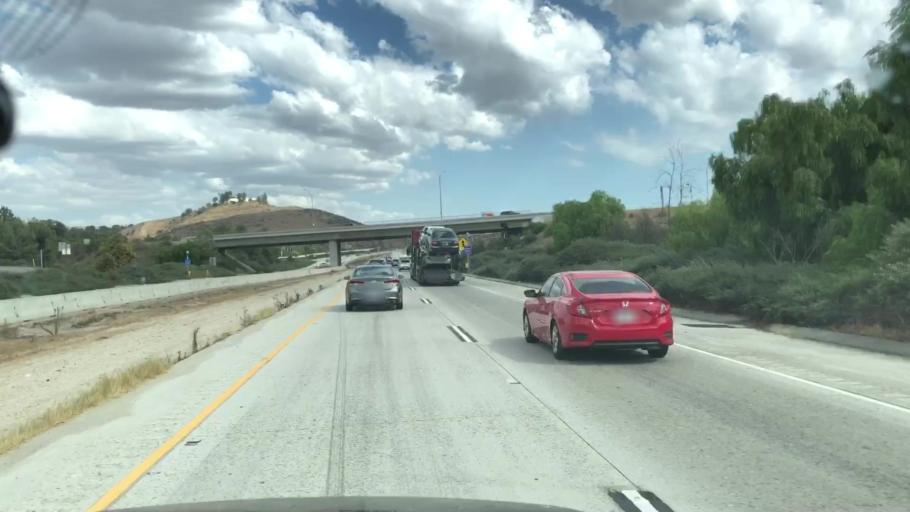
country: US
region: California
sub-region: Ventura County
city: Moorpark
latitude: 34.2932
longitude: -118.8448
